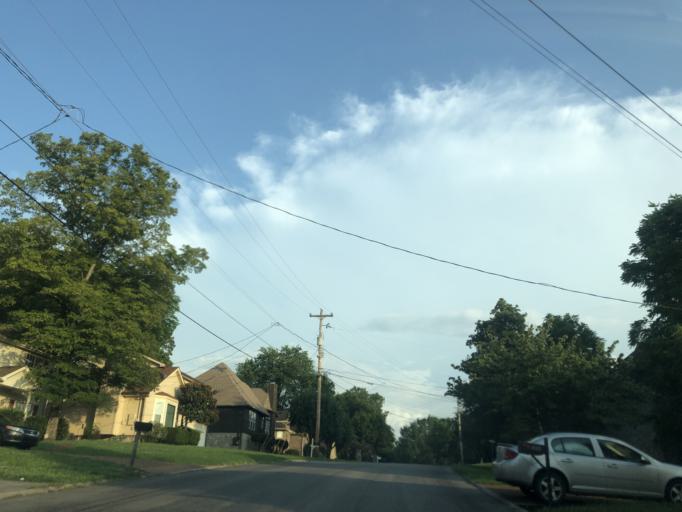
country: US
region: Tennessee
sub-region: Davidson County
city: Lakewood
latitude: 36.1372
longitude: -86.6370
